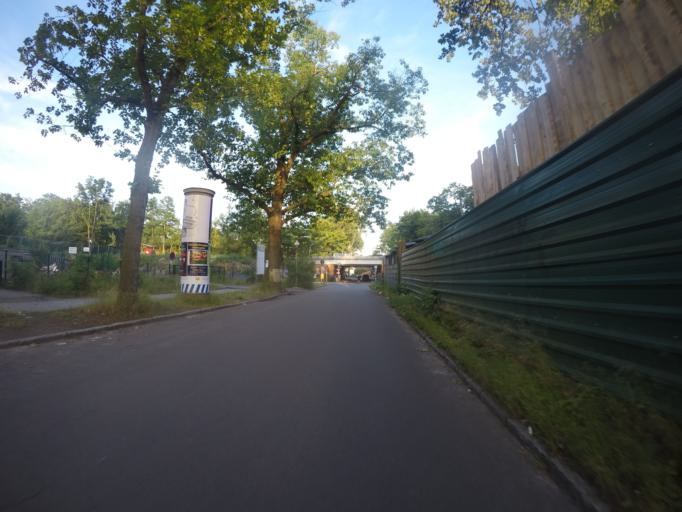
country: DE
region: Berlin
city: Grunewald
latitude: 52.4897
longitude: 13.2599
